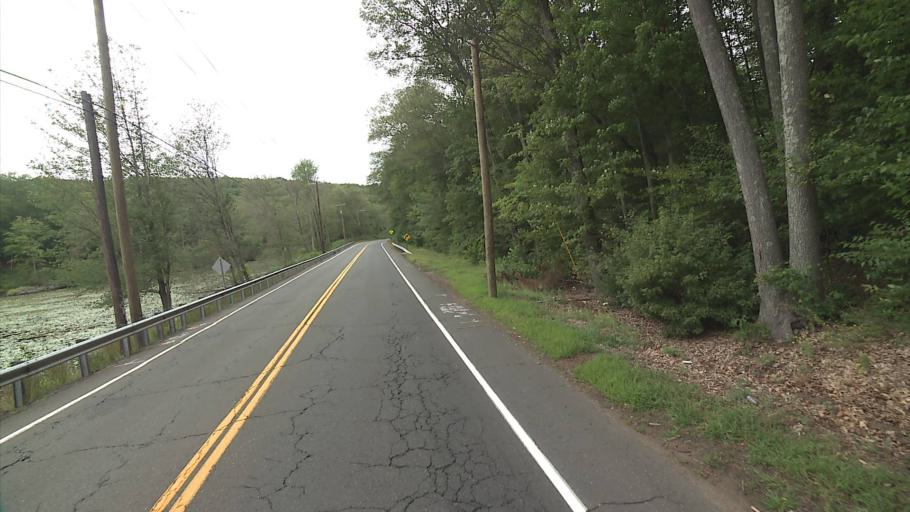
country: US
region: Connecticut
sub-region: Hartford County
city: Manchester
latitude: 41.7613
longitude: -72.4495
